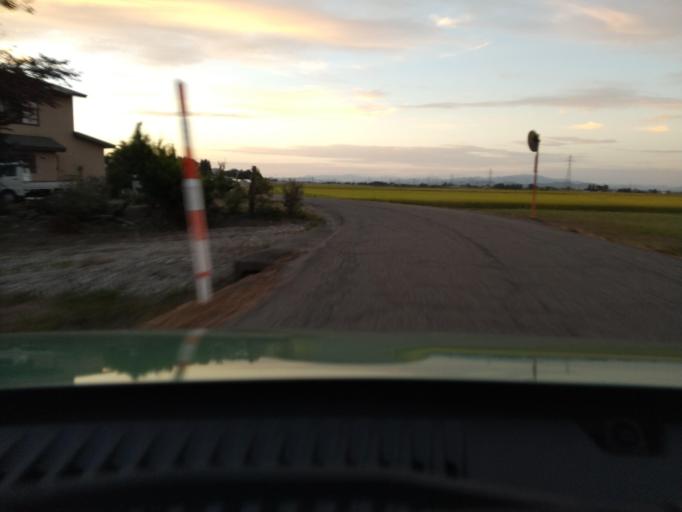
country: JP
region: Akita
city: Omagari
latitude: 39.4031
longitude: 140.5042
